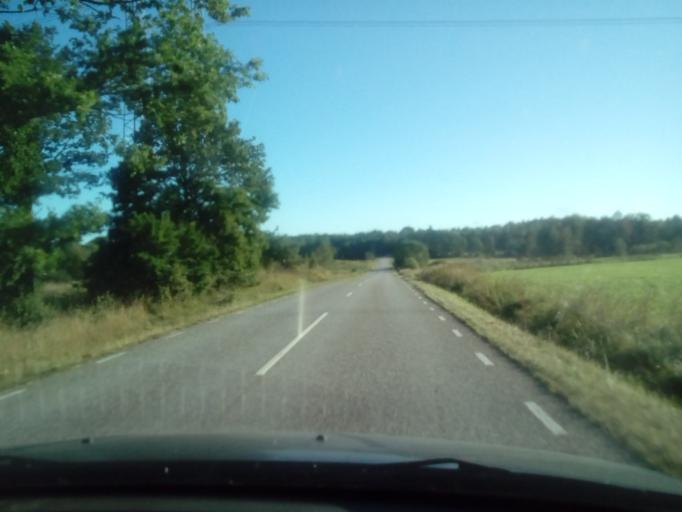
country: SE
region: Kalmar
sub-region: Vasterviks Kommun
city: Ankarsrum
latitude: 57.7943
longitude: 16.3311
